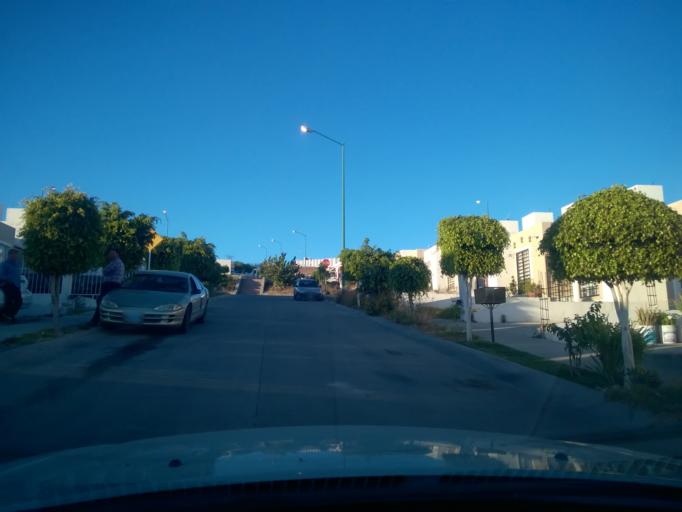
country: MX
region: Guanajuato
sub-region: Leon
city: La Ermita
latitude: 21.1590
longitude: -101.7400
